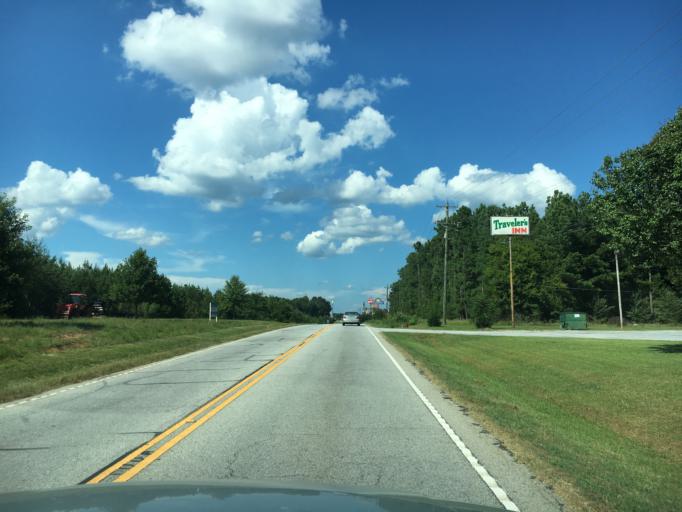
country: US
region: South Carolina
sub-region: Laurens County
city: Clinton
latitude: 34.4995
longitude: -81.8629
